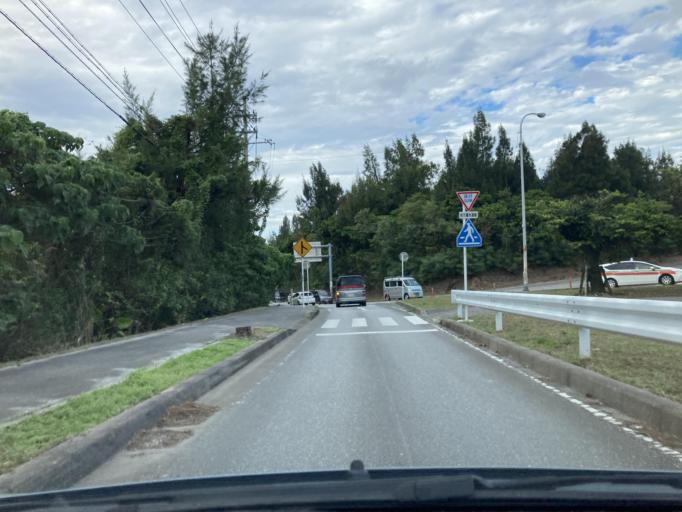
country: JP
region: Okinawa
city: Ishikawa
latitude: 26.4341
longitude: 127.8075
